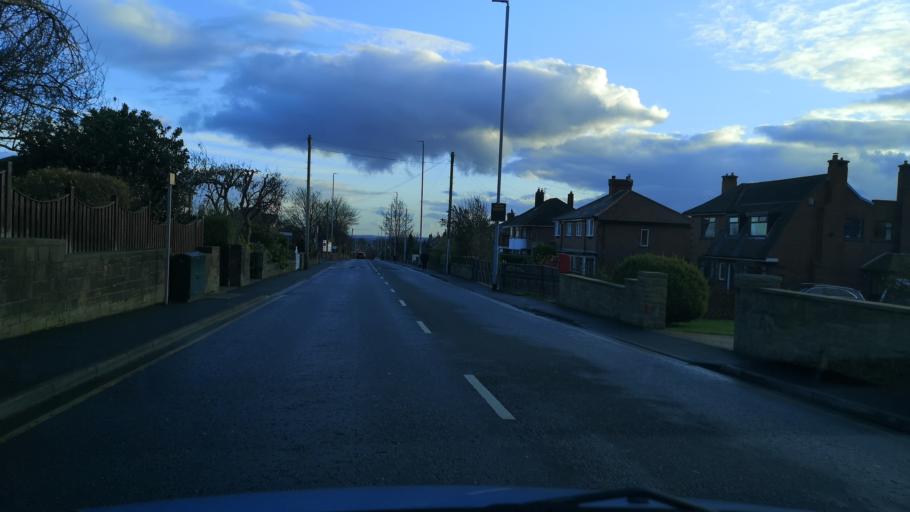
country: GB
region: England
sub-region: City and Borough of Leeds
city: Morley
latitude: 53.7298
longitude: -1.5881
